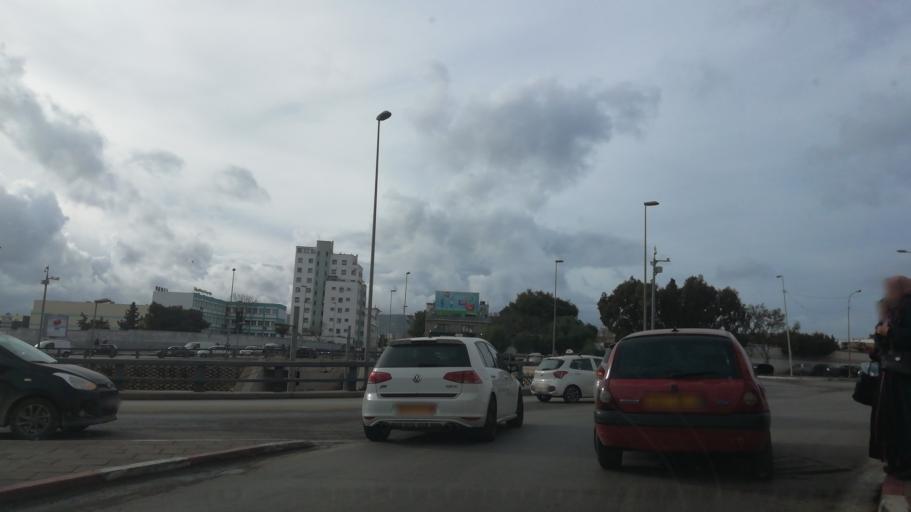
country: DZ
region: Oran
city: Oran
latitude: 35.6971
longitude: -0.6126
